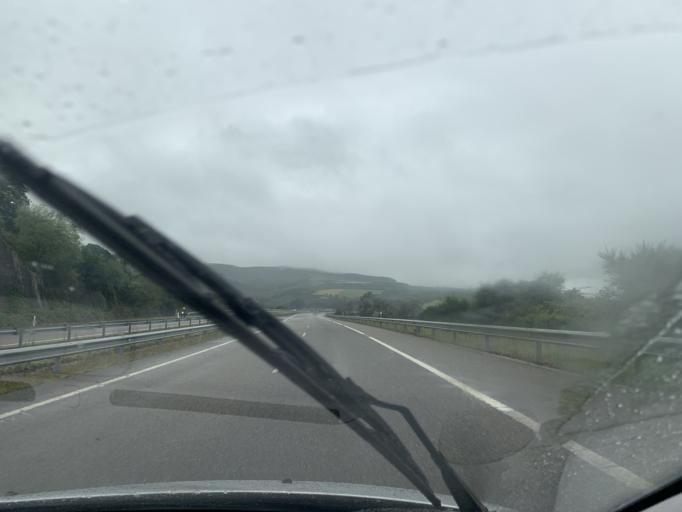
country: ES
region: Galicia
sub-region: Provincia de Lugo
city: Abadin
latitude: 43.3703
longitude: -7.4464
